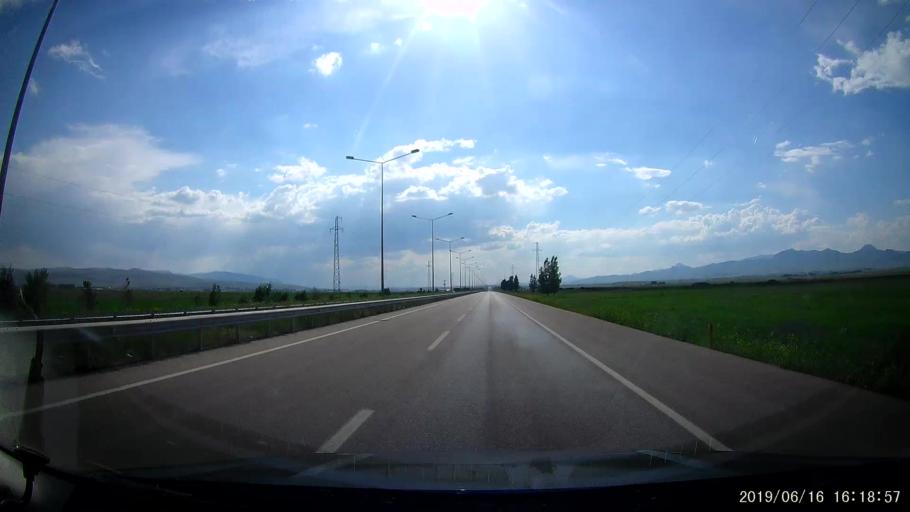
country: TR
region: Erzurum
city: Ilica
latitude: 39.9657
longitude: 41.1539
